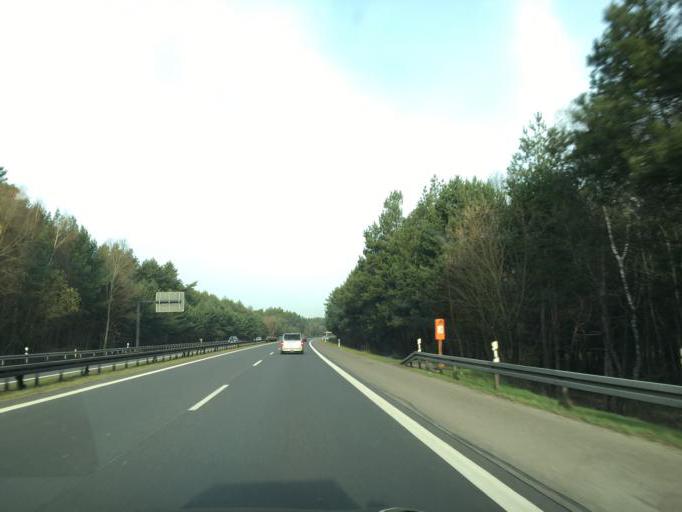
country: DE
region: Brandenburg
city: Glienicke
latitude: 52.6822
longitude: 13.3522
